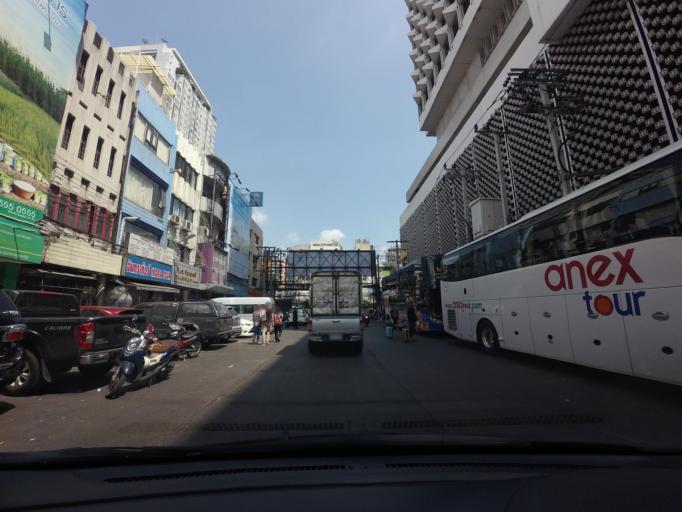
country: TH
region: Bangkok
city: Ratchathewi
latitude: 13.7538
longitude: 100.5414
